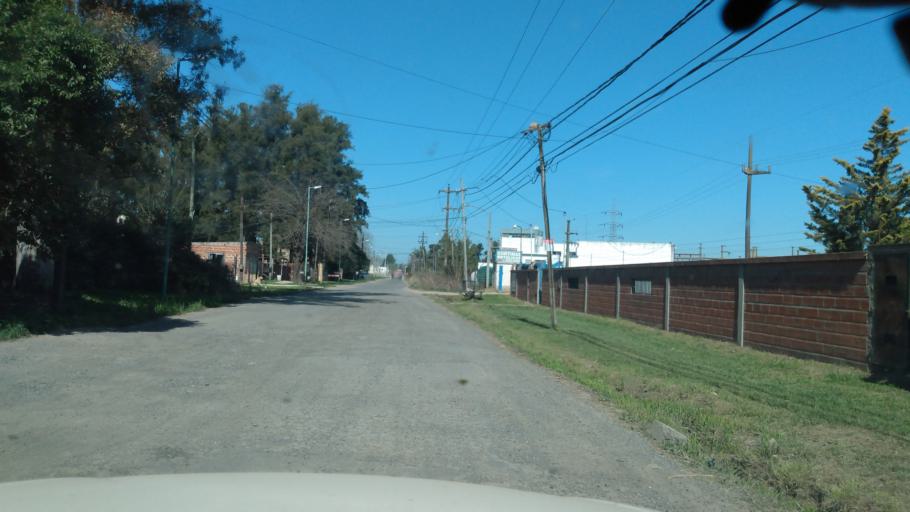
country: AR
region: Buenos Aires
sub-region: Partido de Lujan
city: Lujan
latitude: -34.5853
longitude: -59.1170
